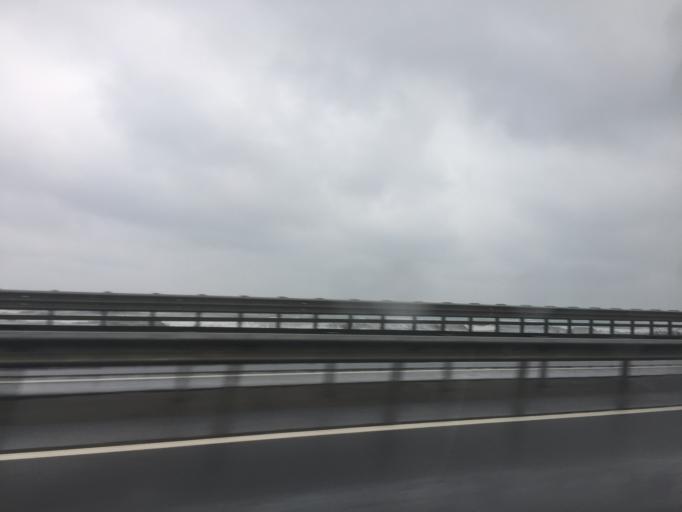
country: TR
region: Zonguldak
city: Alapli
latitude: 41.1062
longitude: 31.2580
